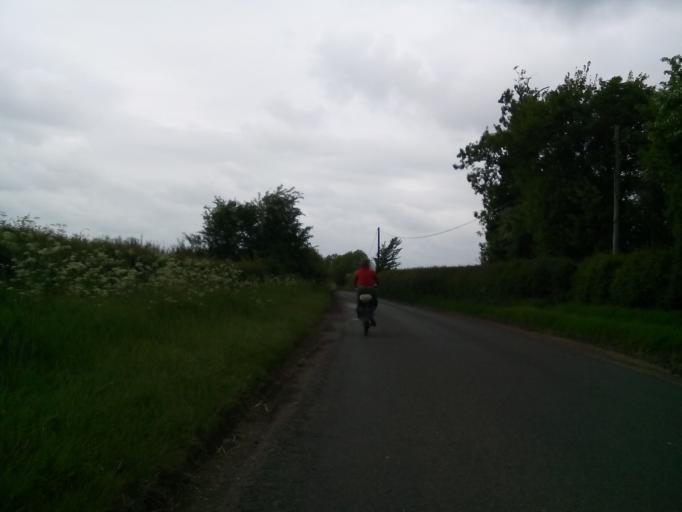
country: GB
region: England
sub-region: District of Rutland
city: South Luffenham
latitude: 52.5313
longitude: -0.5741
